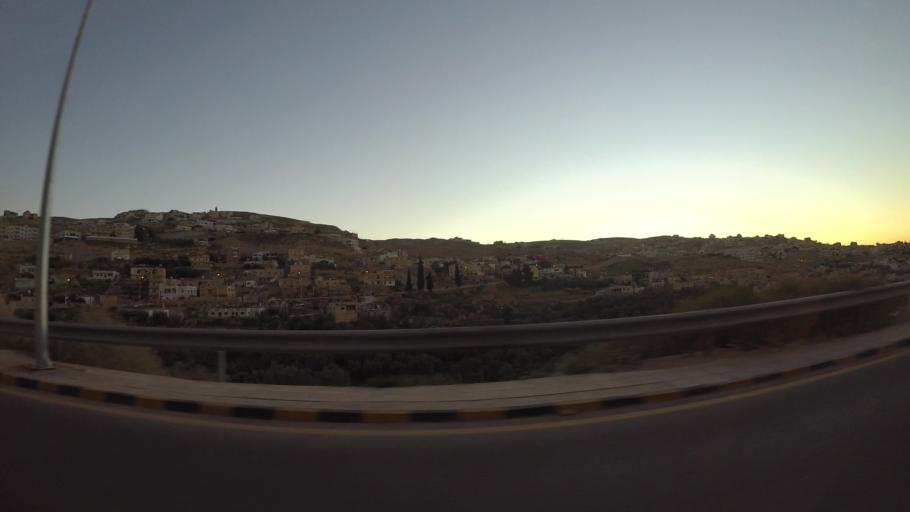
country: JO
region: Ma'an
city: Petra
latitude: 30.3131
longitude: 35.4843
